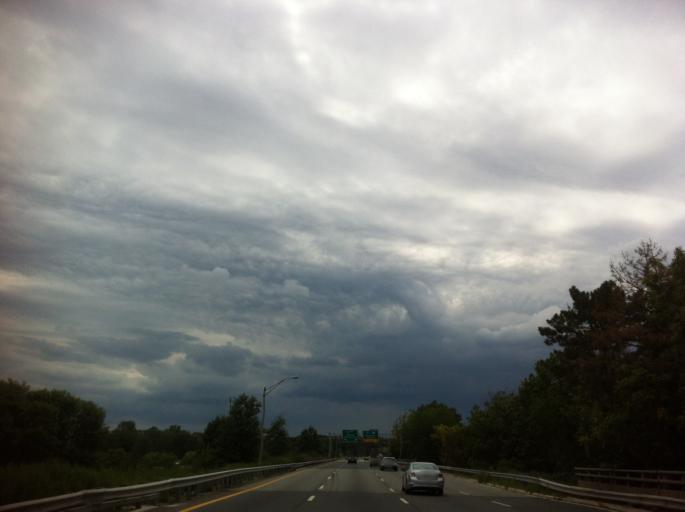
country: US
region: New Jersey
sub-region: Essex County
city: Fairfield
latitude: 40.8662
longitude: -74.3320
